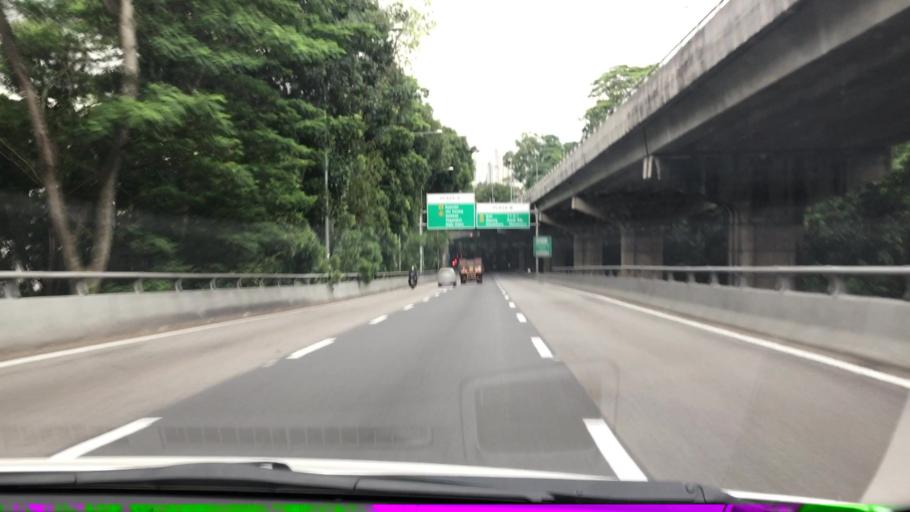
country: MY
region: Kuala Lumpur
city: Kuala Lumpur
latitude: 3.1223
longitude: 101.6613
